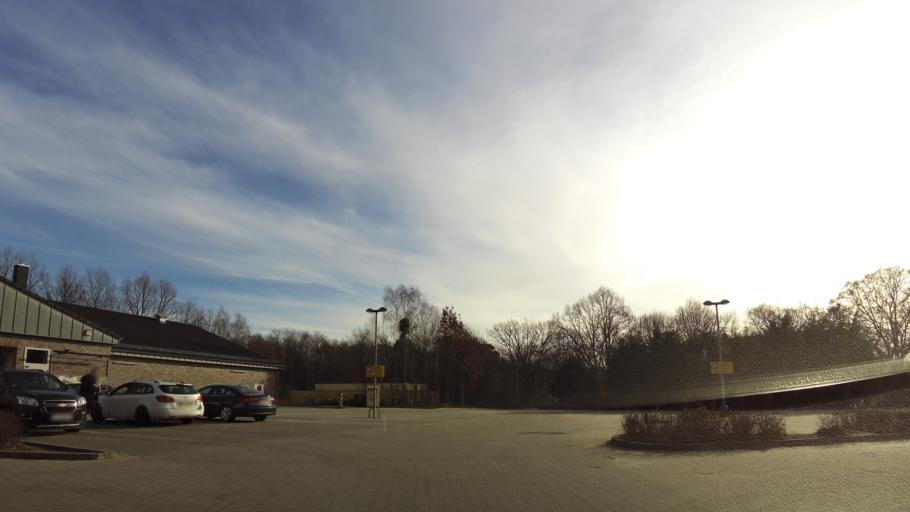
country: DE
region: Brandenburg
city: Michendorf
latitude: 52.3168
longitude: 13.0325
